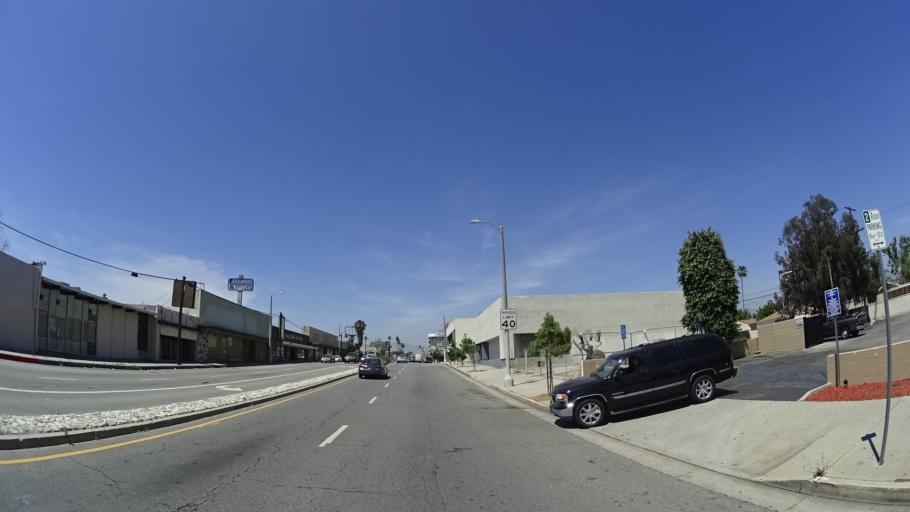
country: US
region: California
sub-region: Los Angeles County
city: North Hollywood
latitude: 34.1833
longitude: -118.3965
